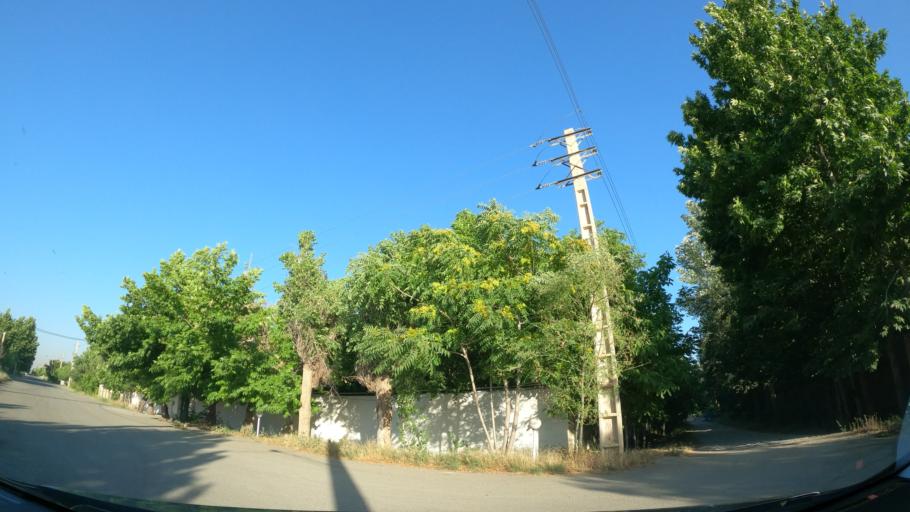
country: IR
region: Alborz
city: Hashtgerd
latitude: 35.9112
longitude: 50.7211
